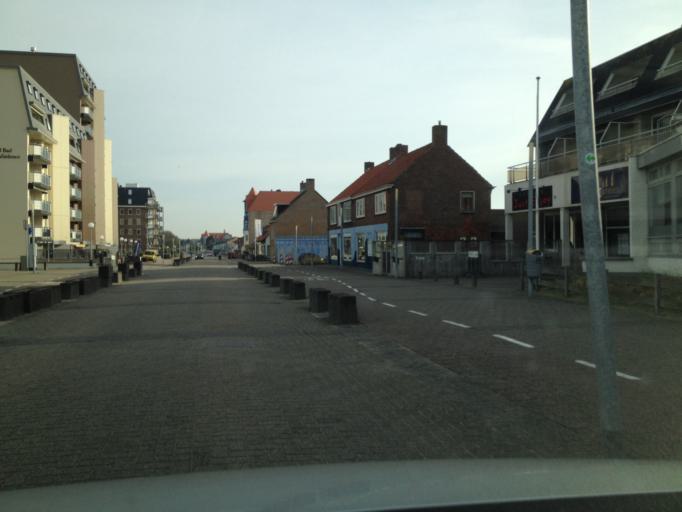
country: NL
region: Zeeland
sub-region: Gemeente Sluis
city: Sluis
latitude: 51.3774
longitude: 3.3831
